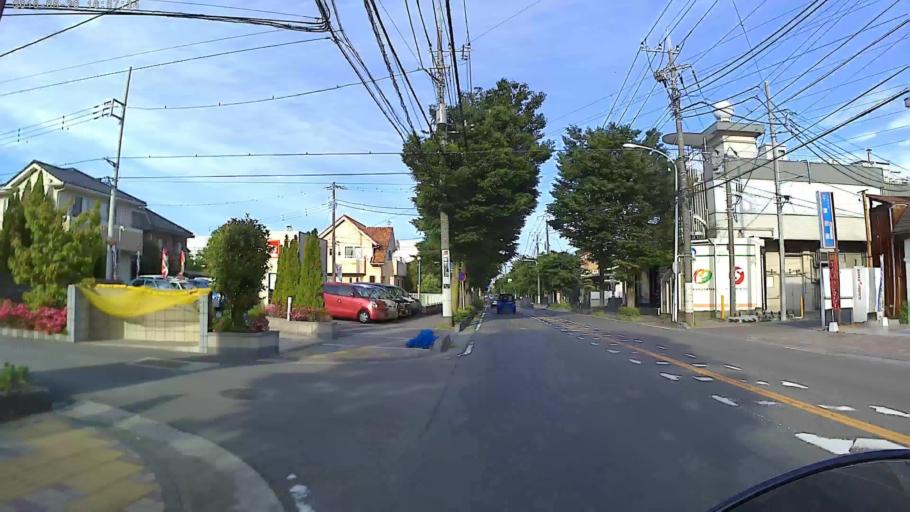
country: JP
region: Kanagawa
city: Odawara
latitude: 35.2800
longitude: 139.1745
